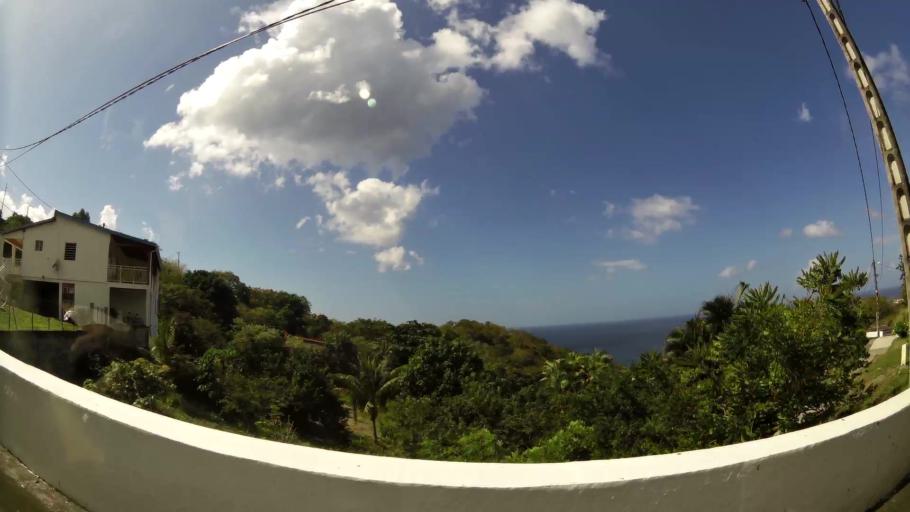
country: MQ
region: Martinique
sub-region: Martinique
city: Saint-Pierre
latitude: 14.6934
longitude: -61.1740
